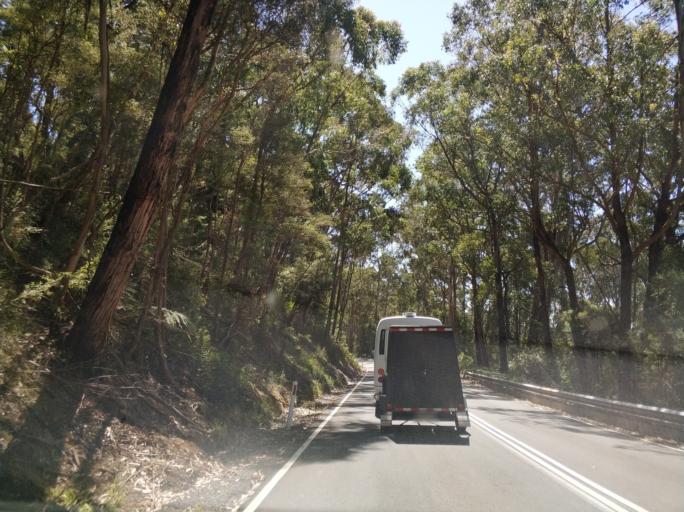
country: AU
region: Victoria
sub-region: Colac-Otway
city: Apollo Bay
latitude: -38.7439
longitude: 143.2563
